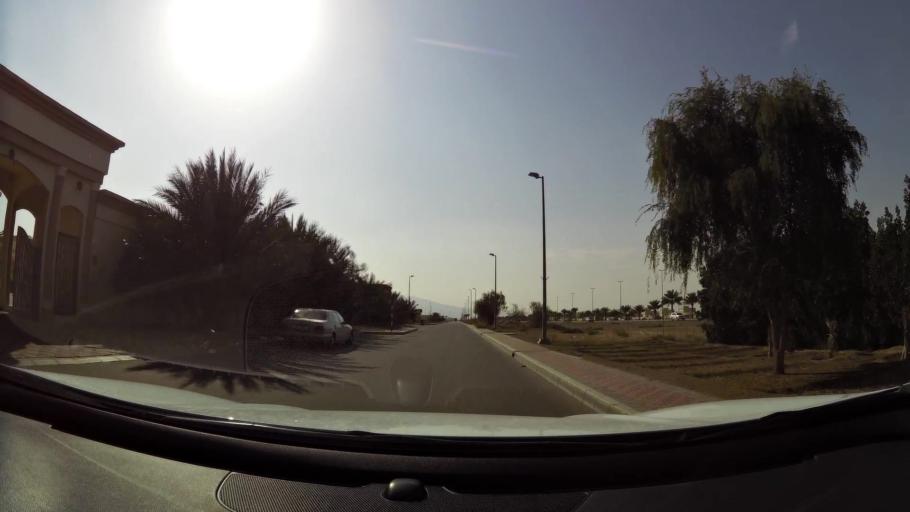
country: AE
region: Abu Dhabi
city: Al Ain
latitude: 24.0926
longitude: 55.9007
